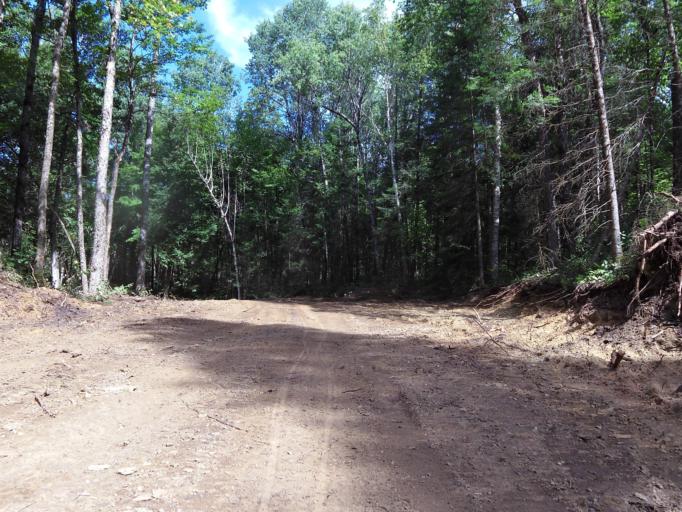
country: CA
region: Ontario
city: Renfrew
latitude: 45.1063
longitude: -76.7169
